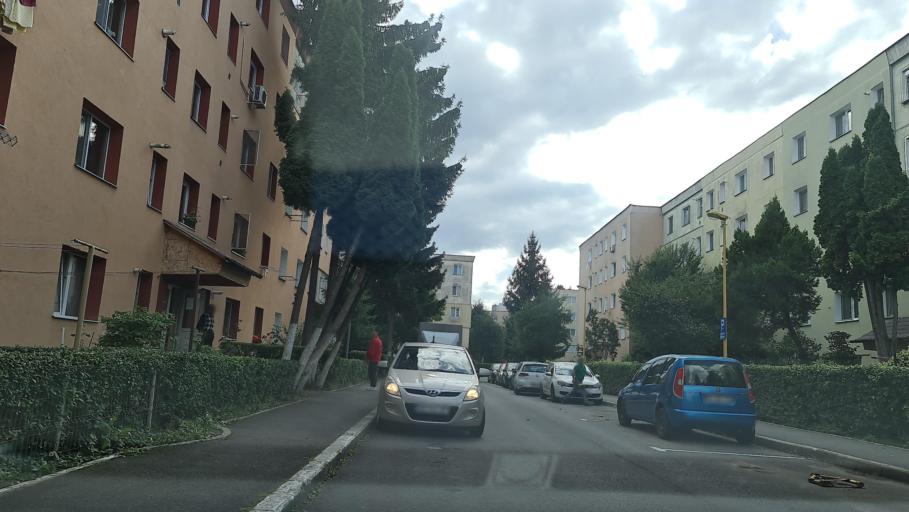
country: RO
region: Brasov
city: Brasov
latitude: 45.6522
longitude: 25.6305
